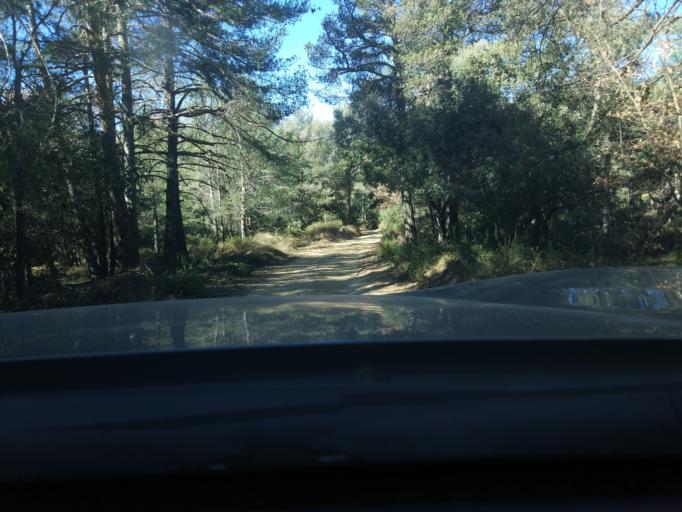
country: ES
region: Aragon
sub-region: Provincia de Huesca
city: Palo
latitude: 42.2940
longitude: 0.3403
